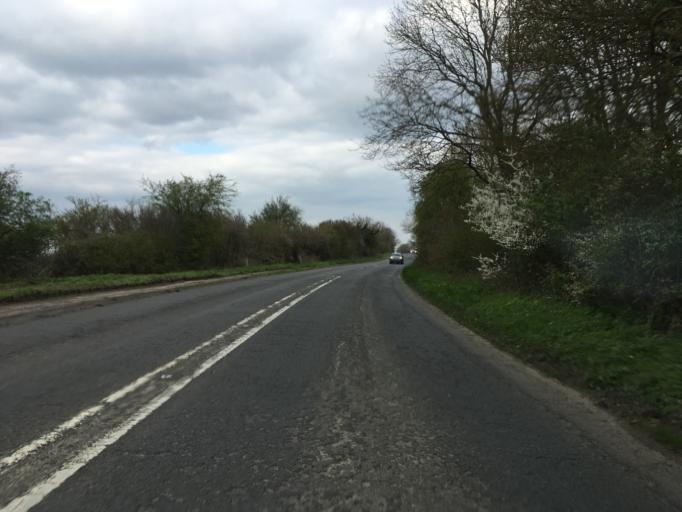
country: GB
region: England
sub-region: Oxfordshire
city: Carterton
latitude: 51.7914
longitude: -1.5655
